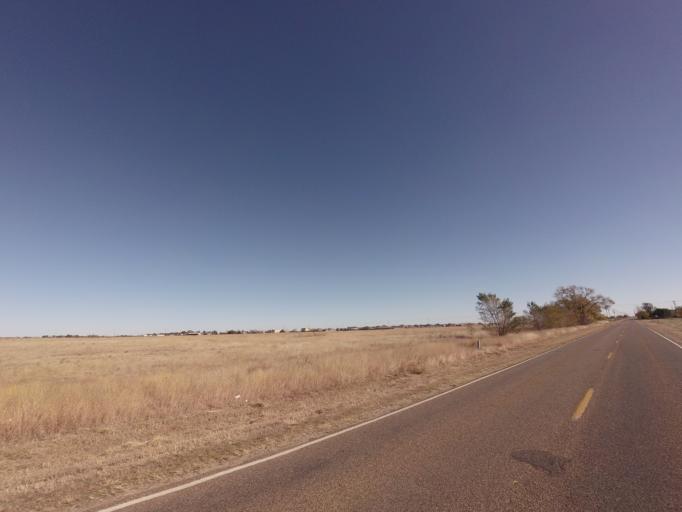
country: US
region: New Mexico
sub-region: Curry County
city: Clovis
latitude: 34.4194
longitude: -103.1637
